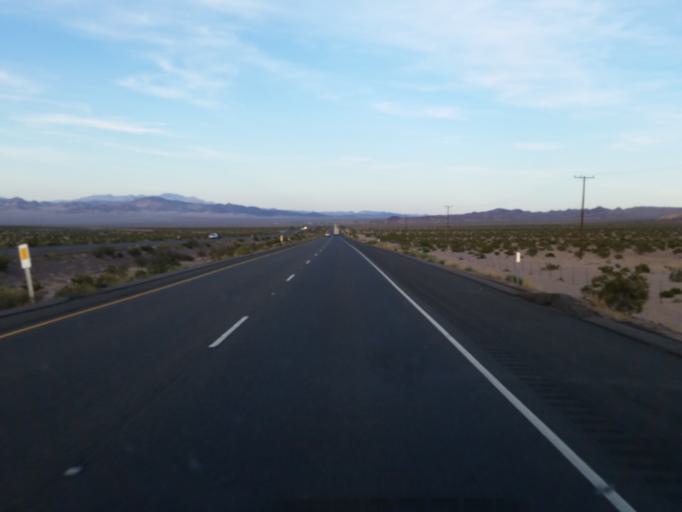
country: US
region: California
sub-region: San Bernardino County
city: Joshua Tree
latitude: 34.7261
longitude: -116.2408
